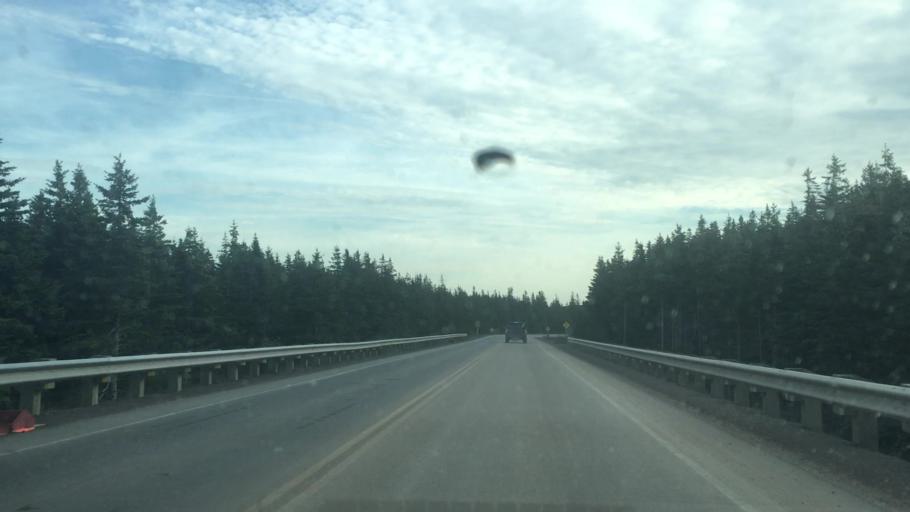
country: CA
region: Nova Scotia
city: Sydney Mines
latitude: 46.8014
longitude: -60.8440
